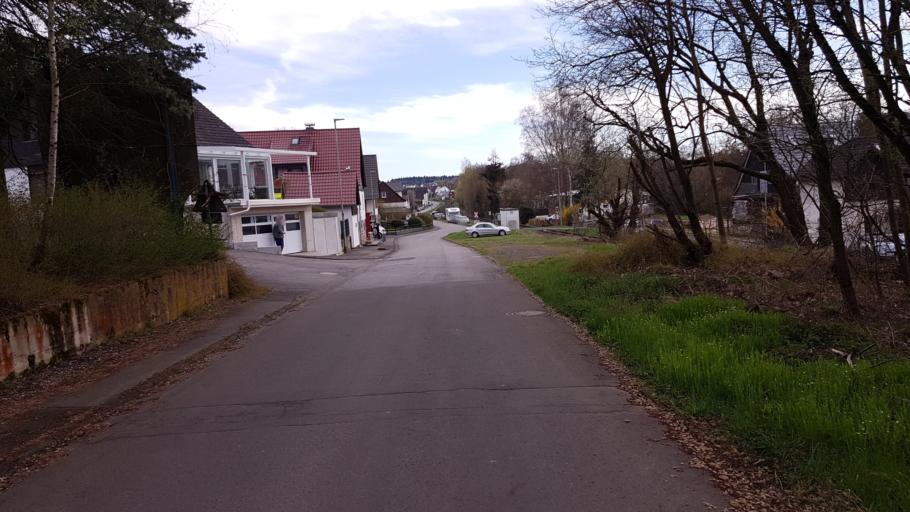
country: DE
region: Hesse
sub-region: Regierungsbezirk Giessen
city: Homberg
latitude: 50.6523
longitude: 9.0349
